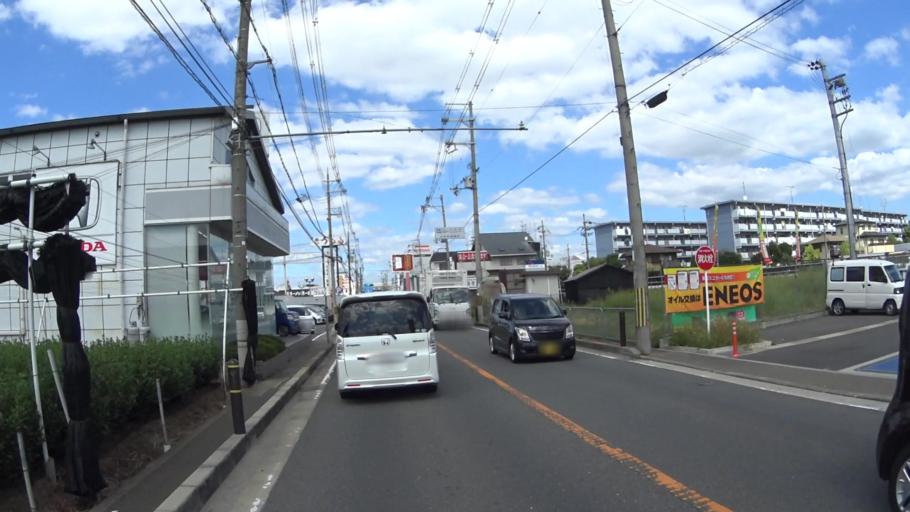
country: JP
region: Kyoto
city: Uji
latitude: 34.9051
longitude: 135.7837
